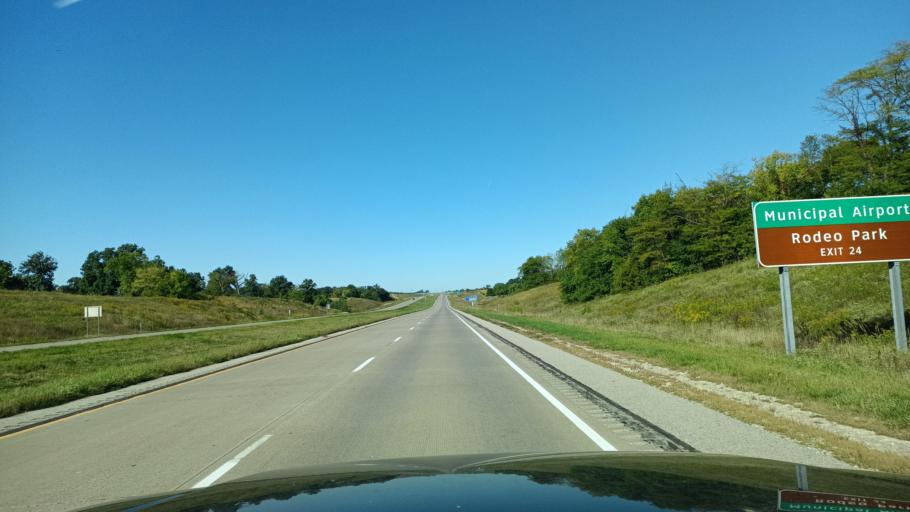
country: US
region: Iowa
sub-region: Lee County
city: Fort Madison
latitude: 40.6707
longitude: -91.3100
